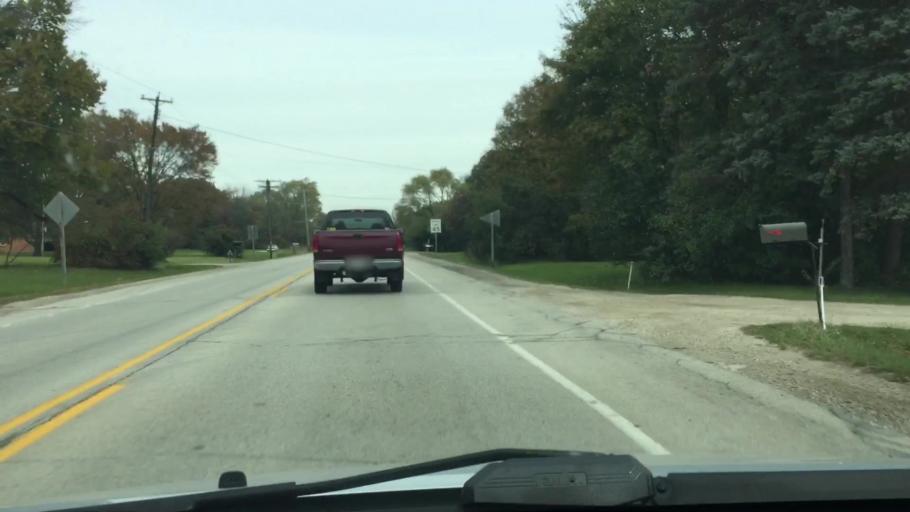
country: US
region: Wisconsin
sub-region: Milwaukee County
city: Franklin
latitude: 42.8947
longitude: -88.0394
